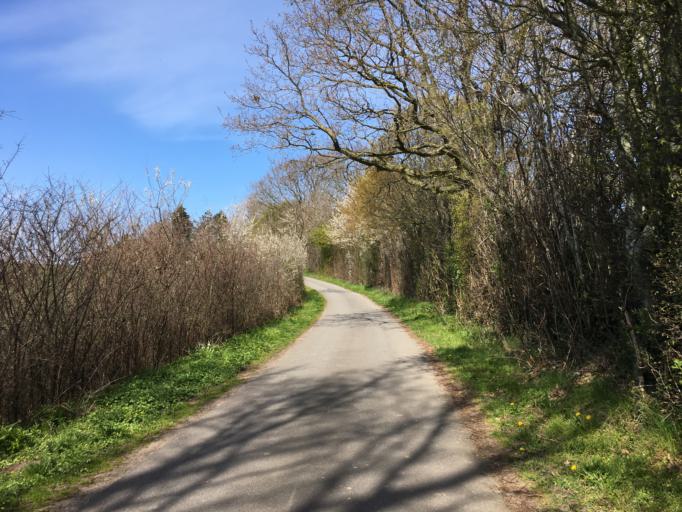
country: DE
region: Schleswig-Holstein
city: Nottfeld
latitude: 54.5919
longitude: 9.7983
